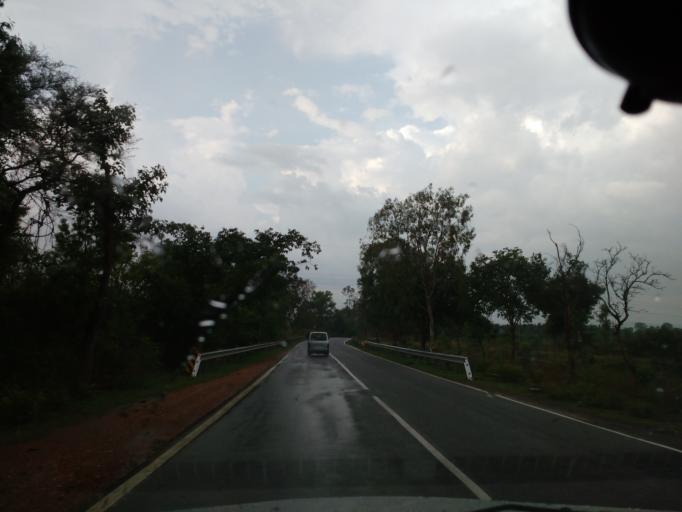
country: IN
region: Karnataka
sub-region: Tumkur
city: Chiknayakanhalli
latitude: 13.2990
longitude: 76.5908
